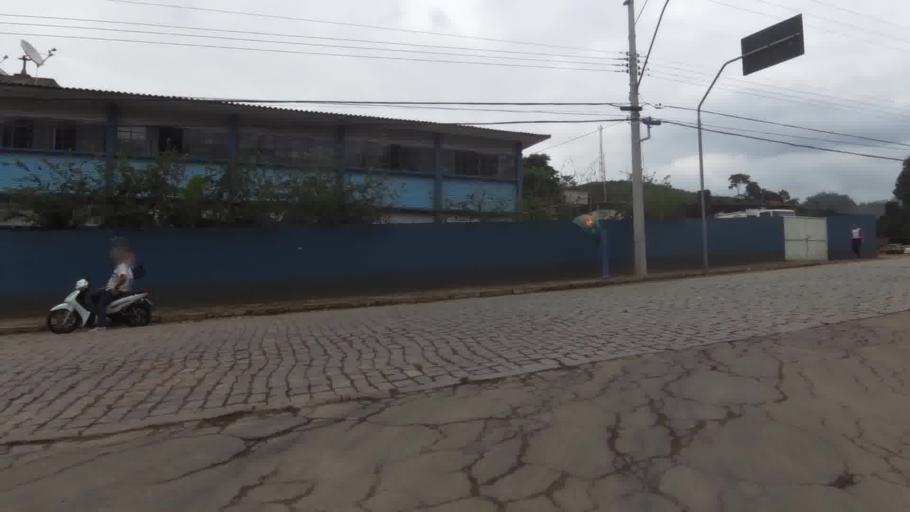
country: BR
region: Espirito Santo
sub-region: Iconha
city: Iconha
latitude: -20.7892
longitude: -40.8159
